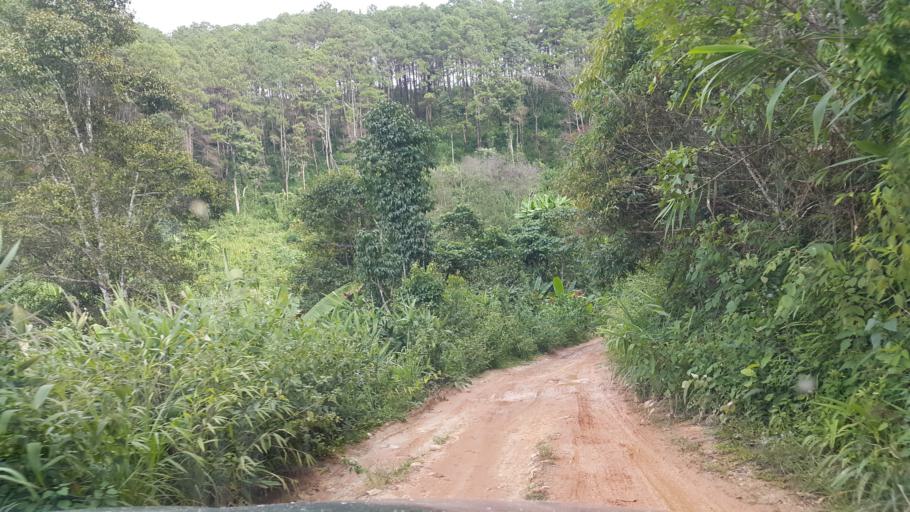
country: TH
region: Chiang Mai
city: Samoeng
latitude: 18.8741
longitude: 98.5038
